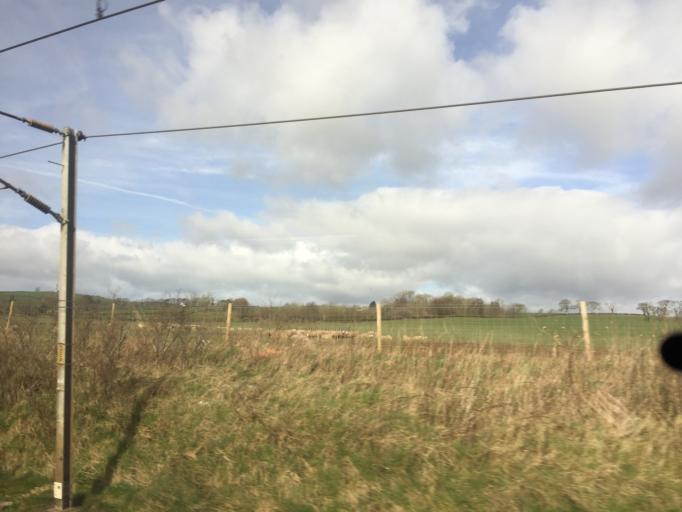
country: GB
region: Scotland
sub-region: Dumfries and Galloway
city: Annan
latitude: 55.0656
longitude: -3.2374
